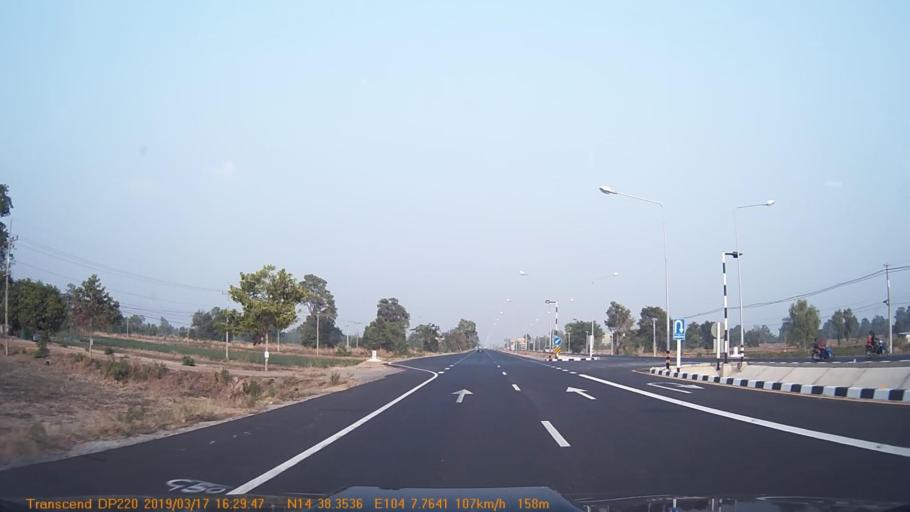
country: TH
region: Sisaket
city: Phu Sing
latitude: 14.6393
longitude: 104.1300
